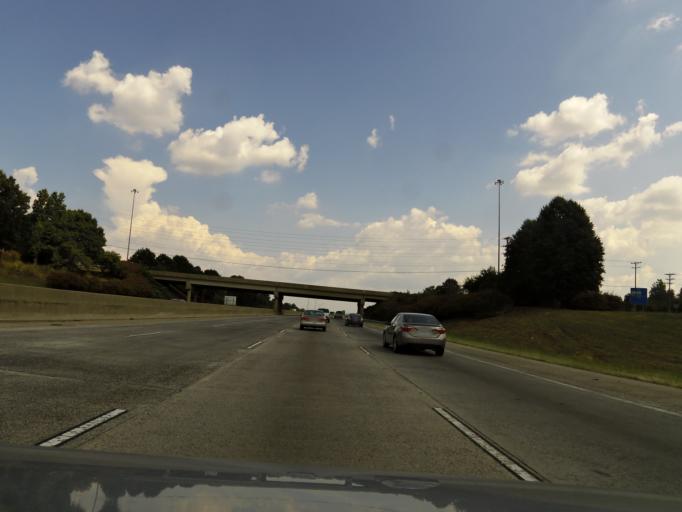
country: US
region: North Carolina
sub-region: Gaston County
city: Mount Holly
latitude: 35.2548
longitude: -80.9841
